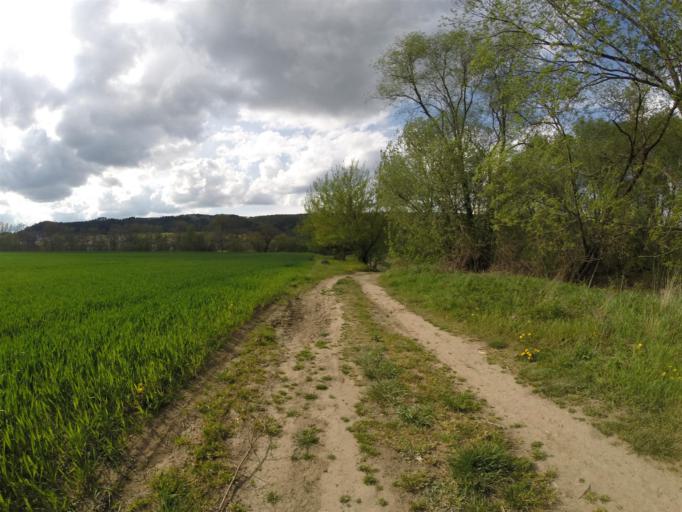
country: DE
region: Thuringia
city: Neuengonna
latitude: 50.9665
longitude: 11.6388
